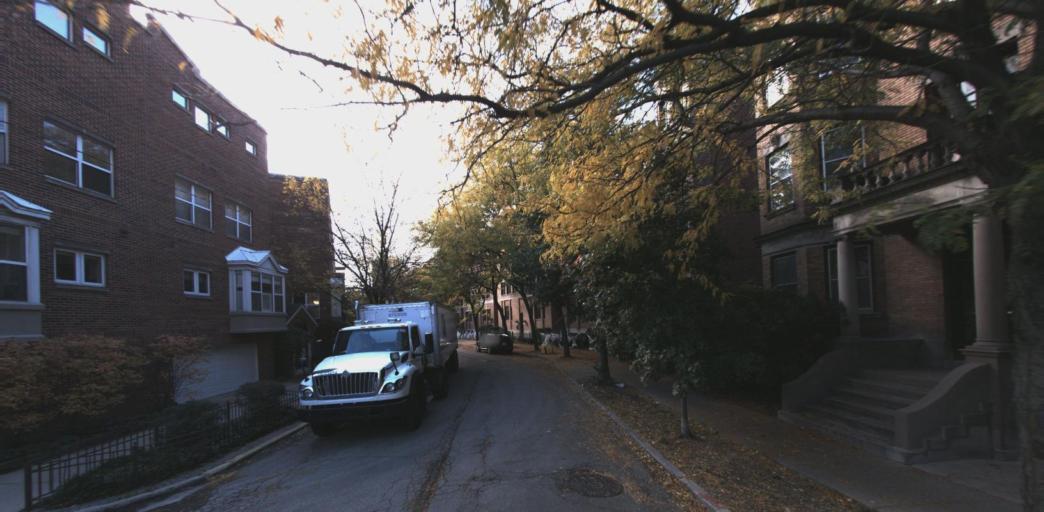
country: US
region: Illinois
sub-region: Cook County
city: Chicago
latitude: 41.9324
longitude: -87.6436
